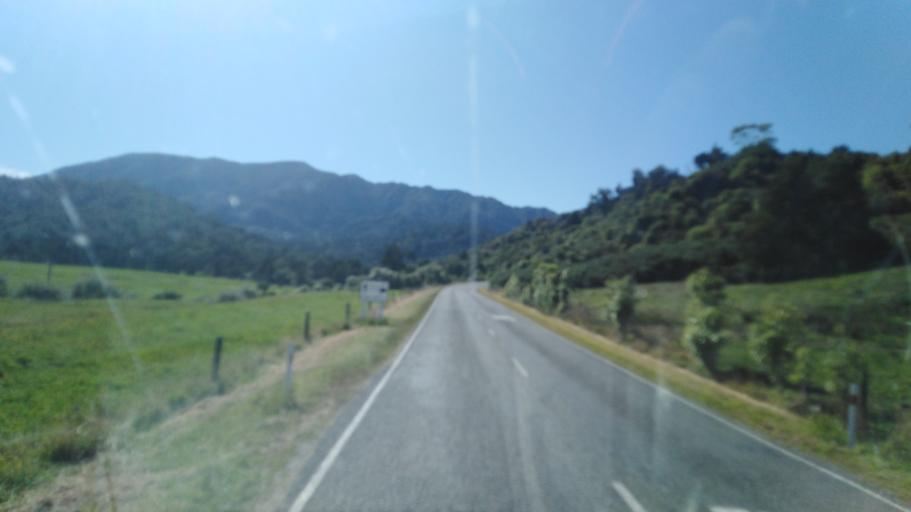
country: NZ
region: West Coast
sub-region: Buller District
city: Westport
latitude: -41.5286
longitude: 171.9708
